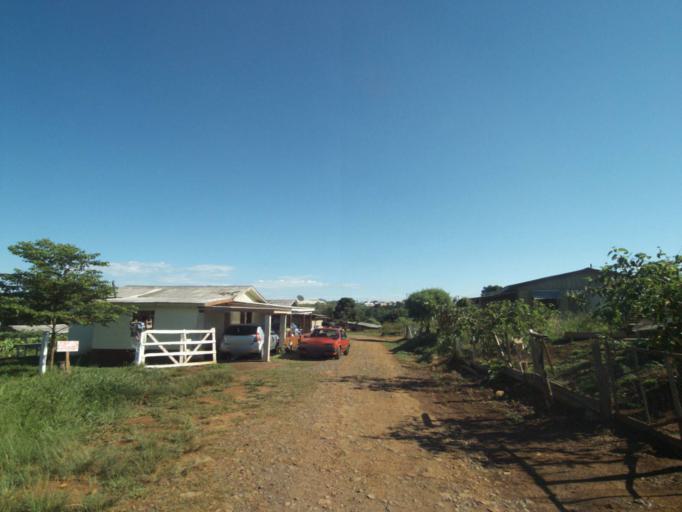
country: BR
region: Parana
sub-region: Pinhao
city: Pinhao
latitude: -25.8415
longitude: -52.0330
